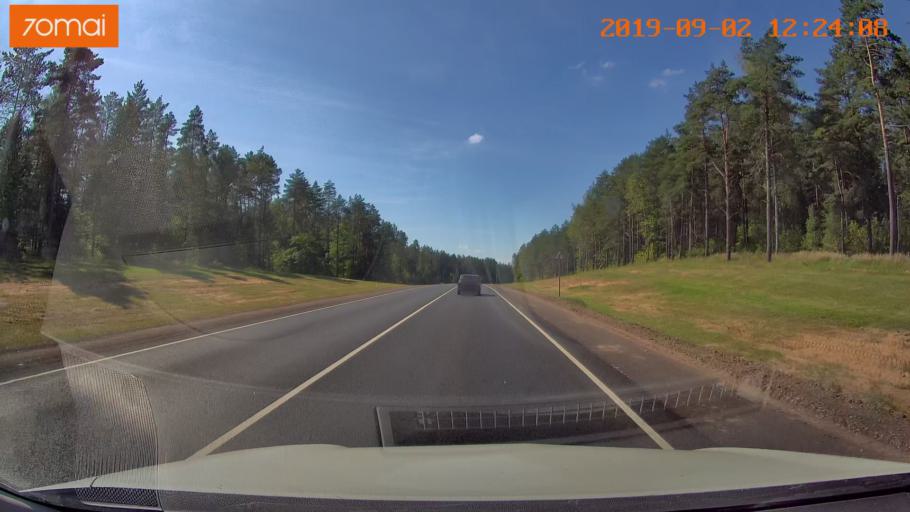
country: RU
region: Smolensk
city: Shumyachi
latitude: 53.8707
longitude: 32.6130
